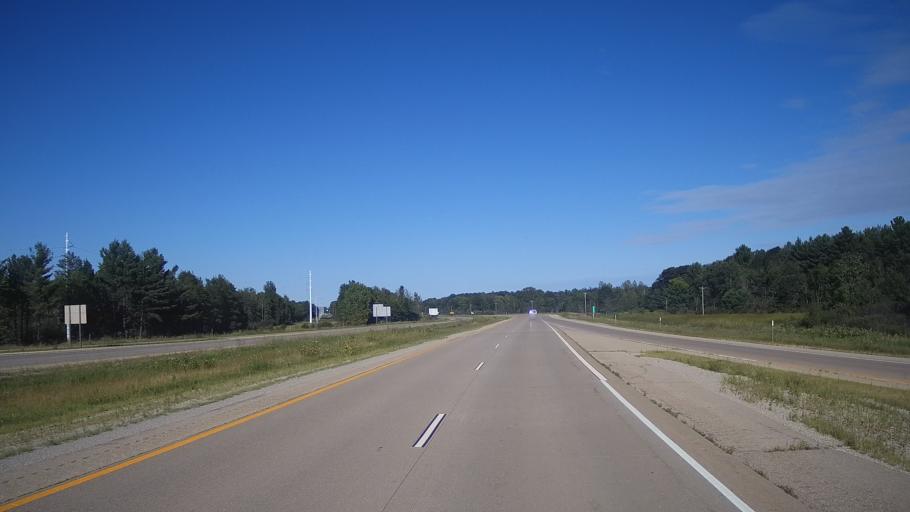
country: US
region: Wisconsin
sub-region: Marinette County
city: Peshtigo
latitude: 45.0611
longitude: -87.7079
